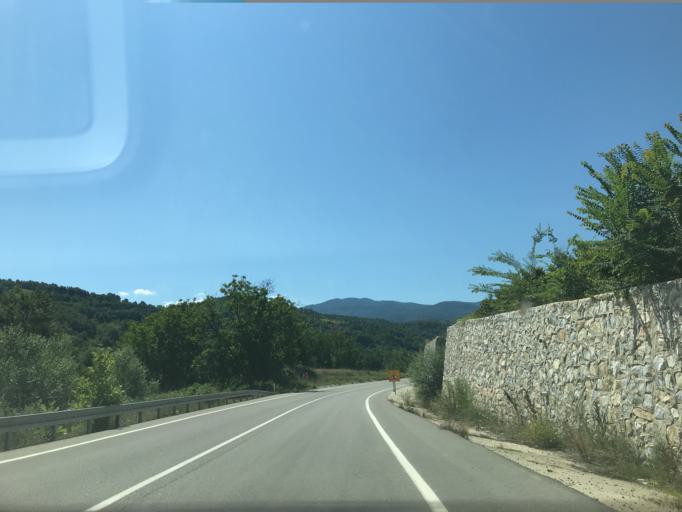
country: TR
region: Bursa
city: Tahtakopru
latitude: 39.9739
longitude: 29.6052
